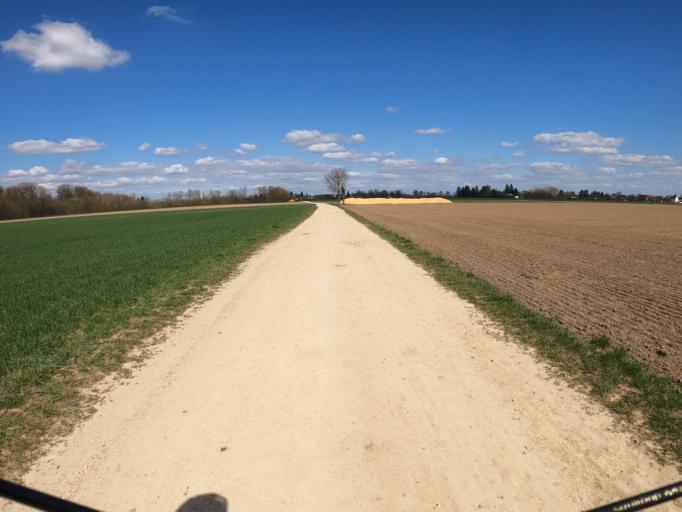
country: DE
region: Bavaria
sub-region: Swabia
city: Nersingen
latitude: 48.4224
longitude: 10.1518
